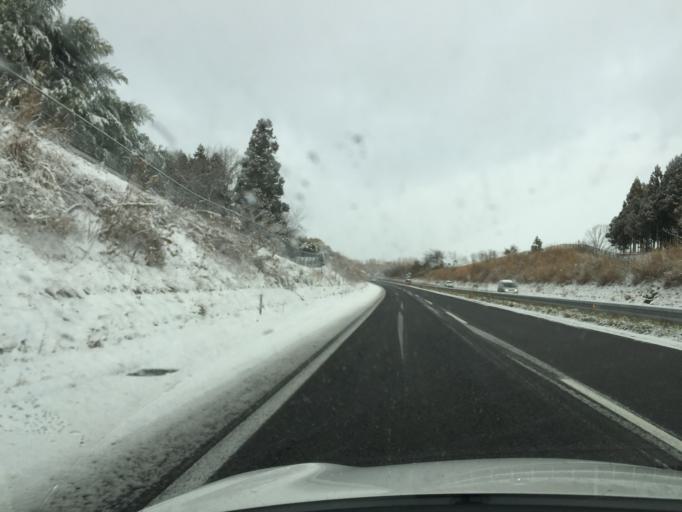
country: JP
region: Fukushima
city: Koriyama
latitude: 37.4481
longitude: 140.4135
